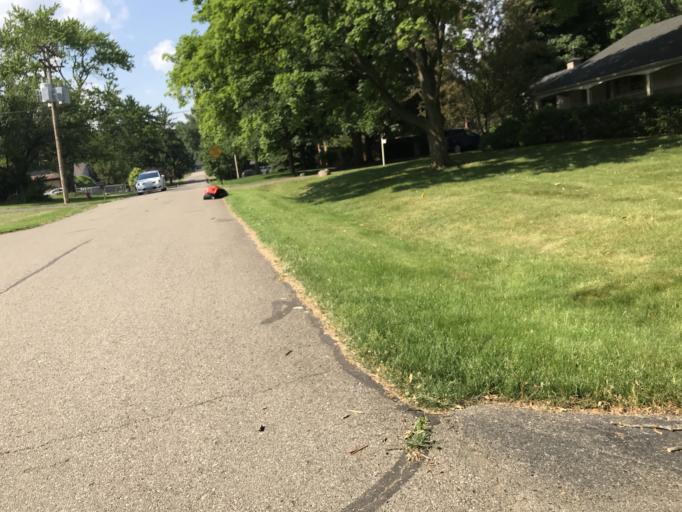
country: US
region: Michigan
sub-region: Oakland County
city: Farmington
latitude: 42.4648
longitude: -83.3903
